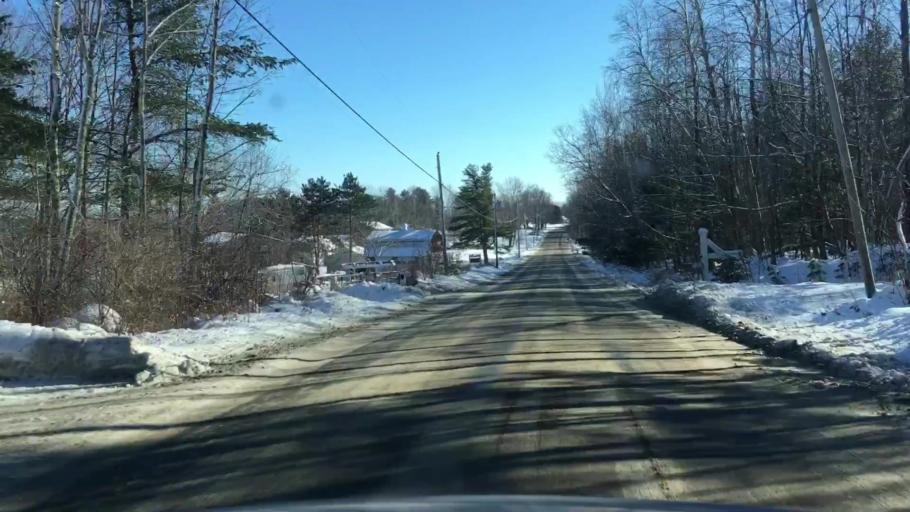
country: US
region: Maine
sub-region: Kennebec County
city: Winthrop
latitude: 44.3366
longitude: -69.9885
